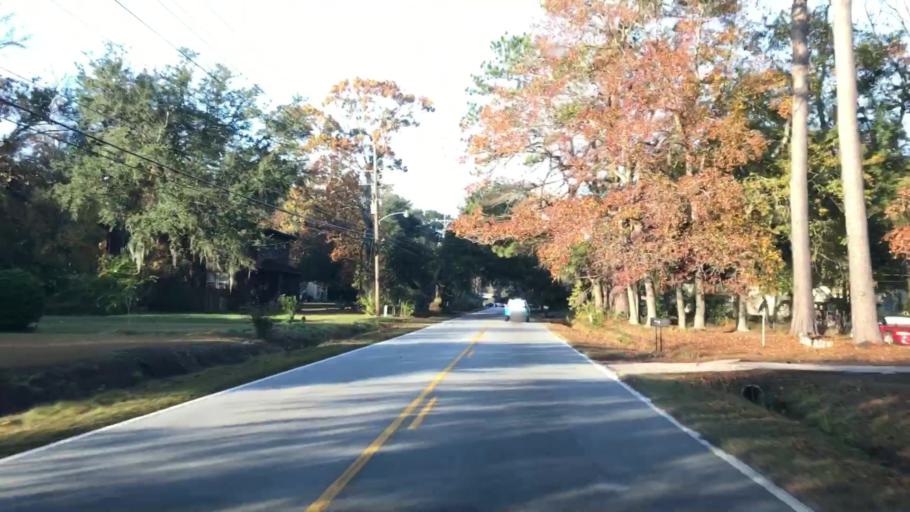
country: US
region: South Carolina
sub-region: Charleston County
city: North Charleston
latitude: 32.8060
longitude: -80.0321
